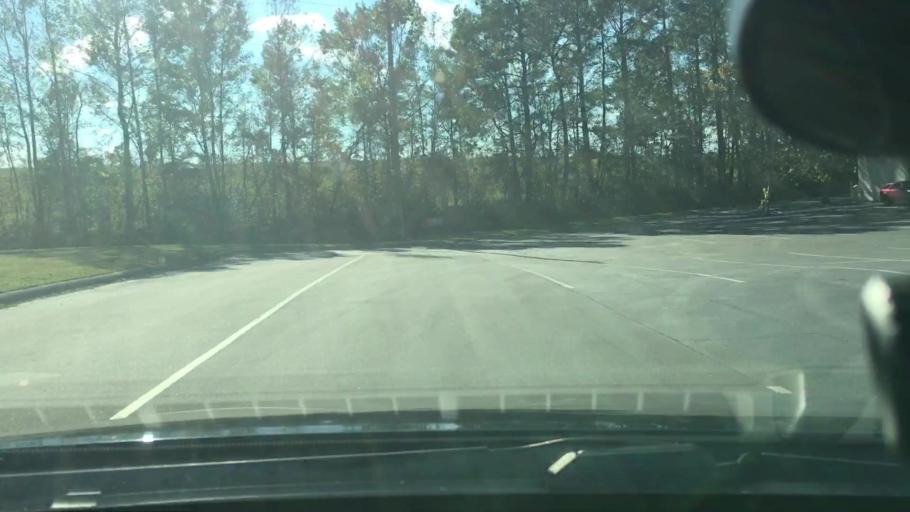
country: US
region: North Carolina
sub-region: Craven County
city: Trent Woods
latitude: 35.1054
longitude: -77.0839
